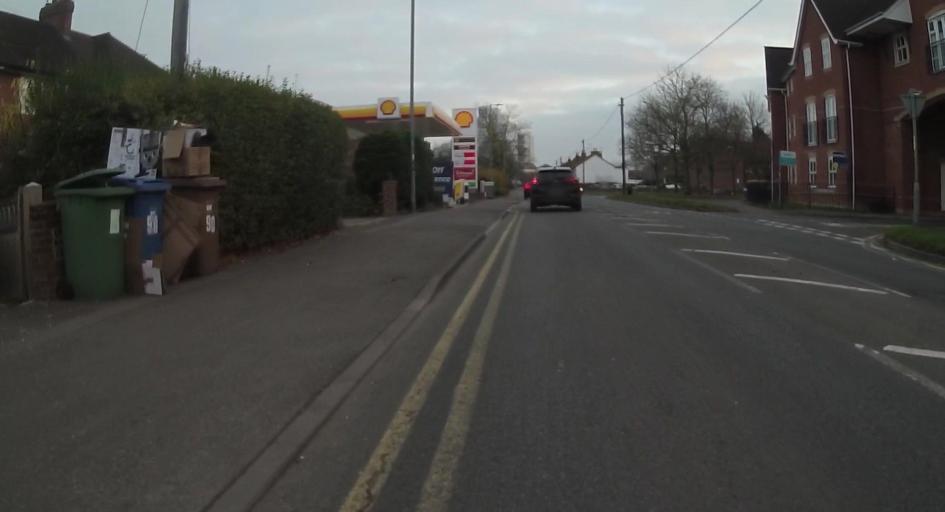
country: GB
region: England
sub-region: Bracknell Forest
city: Bracknell
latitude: 51.4213
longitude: -0.7586
